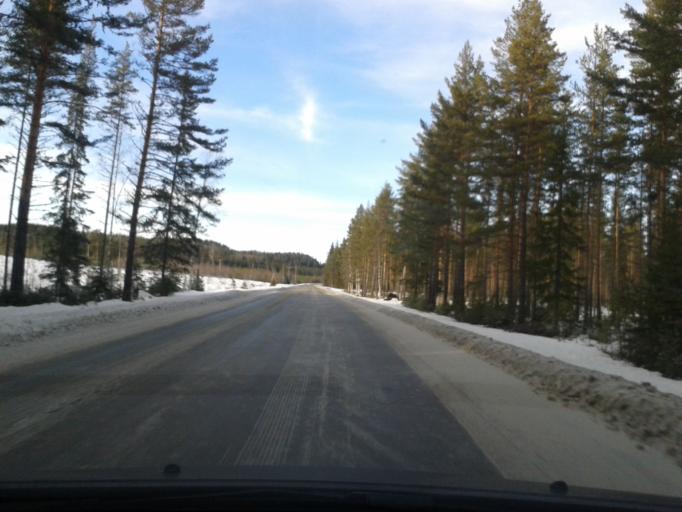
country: SE
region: Vaesternorrland
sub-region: OErnskoeldsviks Kommun
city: Bredbyn
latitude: 63.5497
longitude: 17.9510
